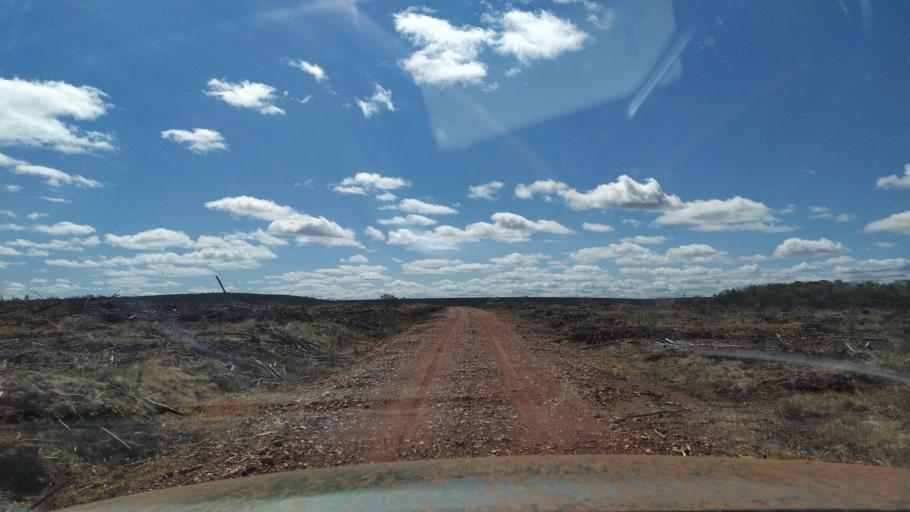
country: AR
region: Corrientes
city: Gobernador Ingeniero Valentin Virasoro
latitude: -28.2956
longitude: -56.0533
